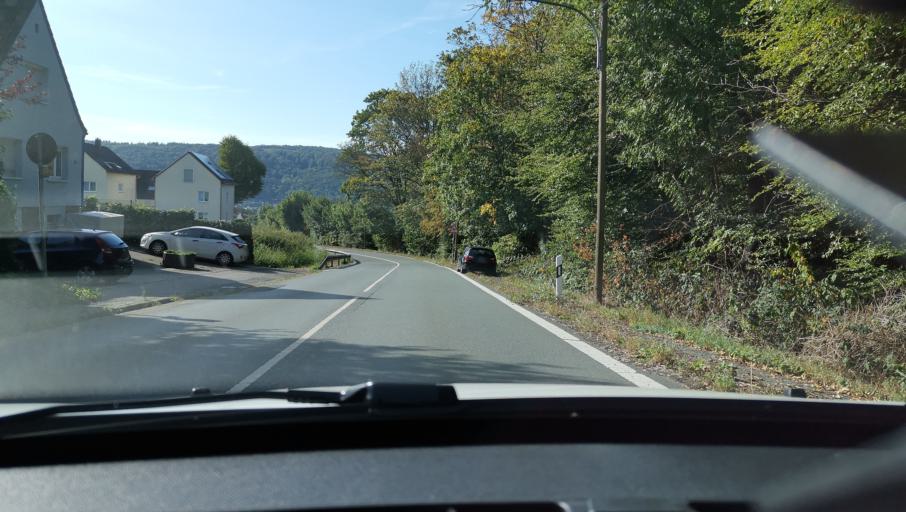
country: DE
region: North Rhine-Westphalia
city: Wetter (Ruhr)
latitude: 51.3463
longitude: 7.3795
